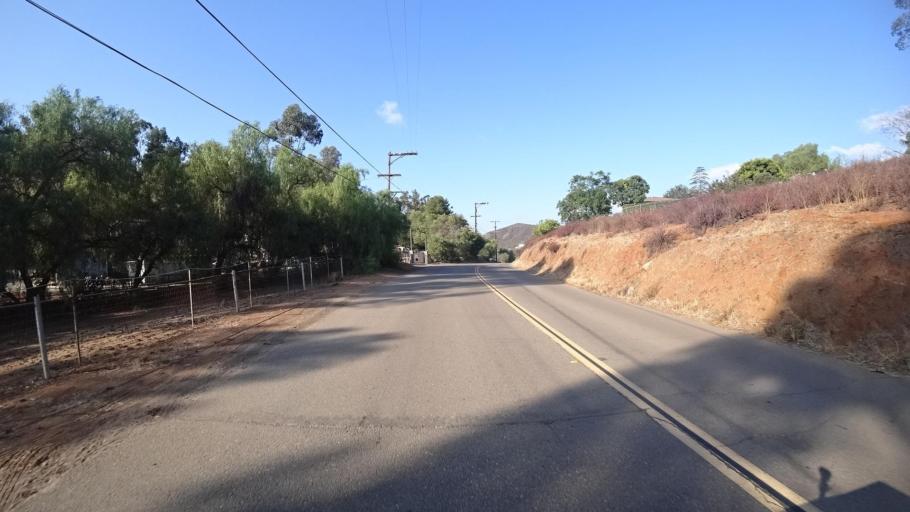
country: US
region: California
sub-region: San Diego County
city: Eucalyptus Hills
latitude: 32.8869
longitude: -116.9511
